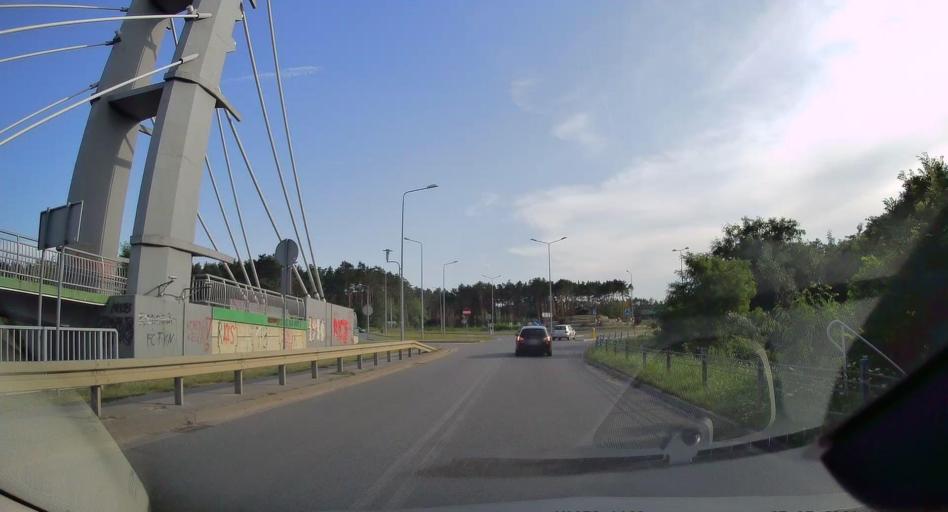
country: PL
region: Swietokrzyskie
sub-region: Powiat konecki
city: Smykow
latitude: 51.1112
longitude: 20.3490
